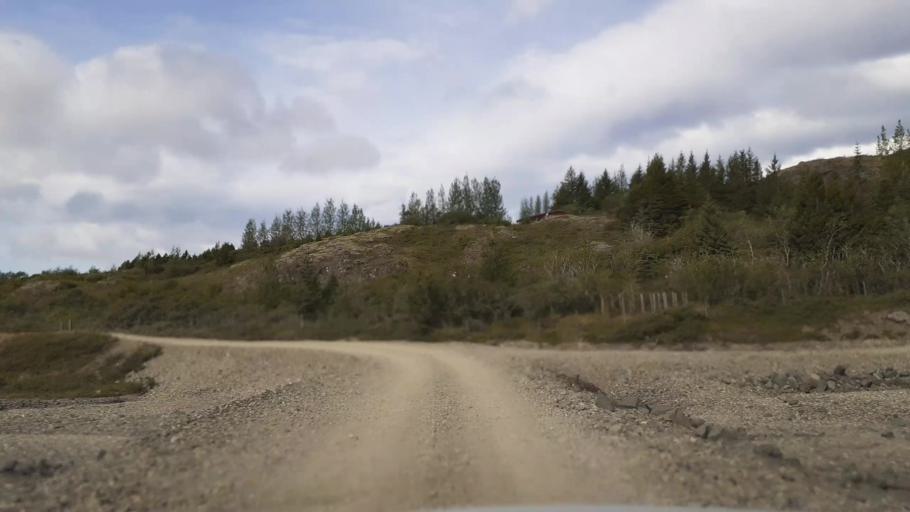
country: IS
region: East
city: Hoefn
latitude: 64.4364
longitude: -14.9034
